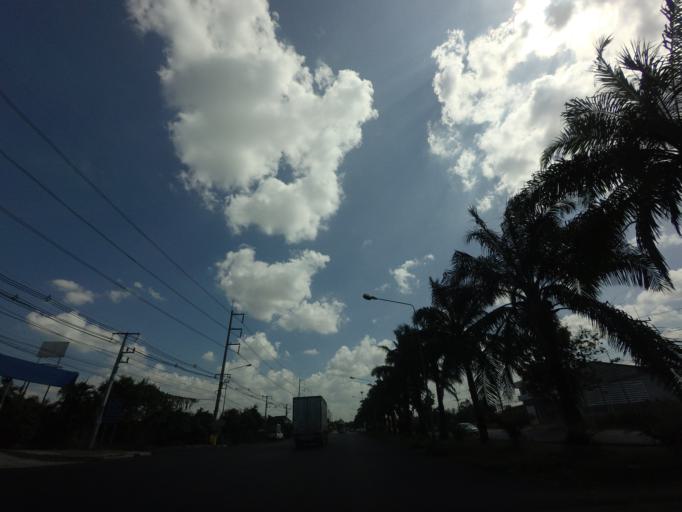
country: TH
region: Chon Buri
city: Ban Bueng
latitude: 13.3078
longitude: 101.1087
